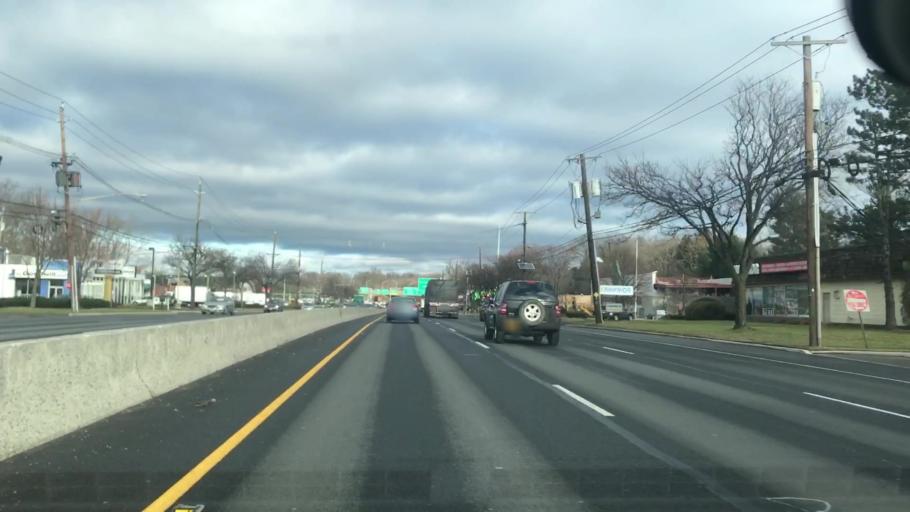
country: US
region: New Jersey
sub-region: Bergen County
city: Ho-Ho-Kus
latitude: 40.9745
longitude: -74.0813
